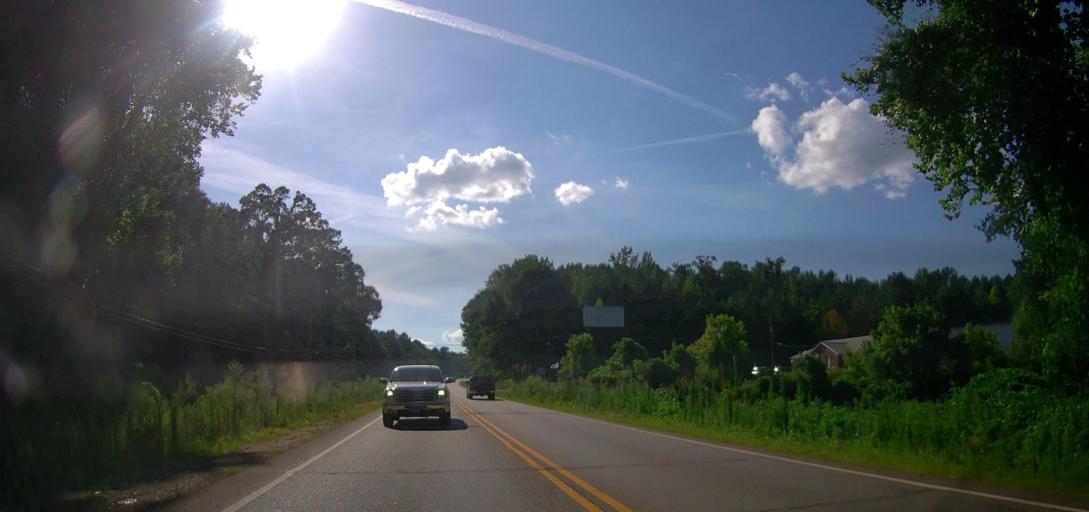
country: US
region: Alabama
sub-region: Tuscaloosa County
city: Holt
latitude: 33.1930
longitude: -87.4701
